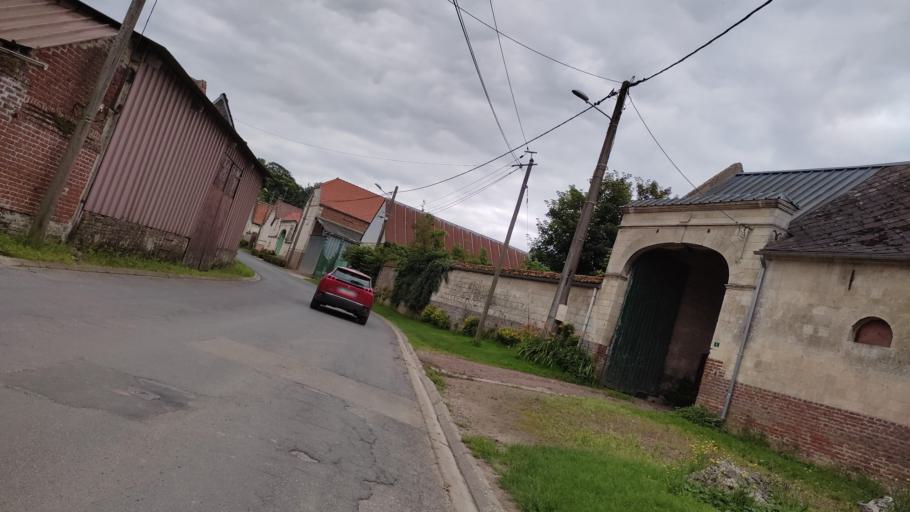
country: FR
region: Nord-Pas-de-Calais
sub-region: Departement du Pas-de-Calais
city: Beaumetz-les-Loges
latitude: 50.2406
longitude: 2.6279
